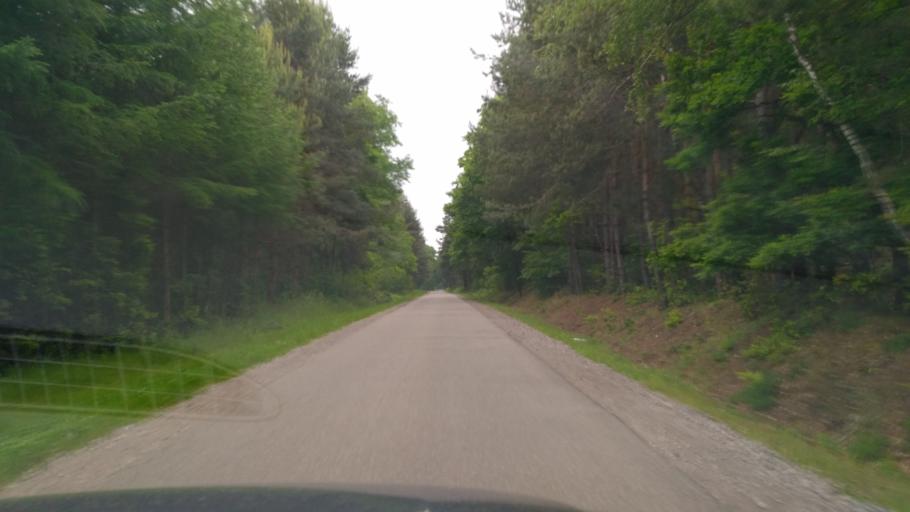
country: PL
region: Subcarpathian Voivodeship
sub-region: Powiat kolbuszowski
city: Niwiska
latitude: 50.2113
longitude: 21.6634
